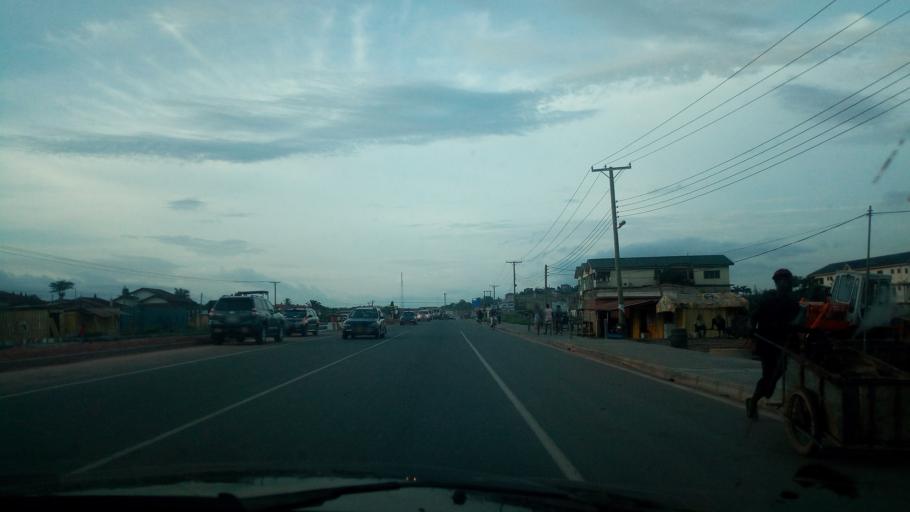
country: GH
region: Western
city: Takoradi
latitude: 4.9275
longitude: -1.7819
